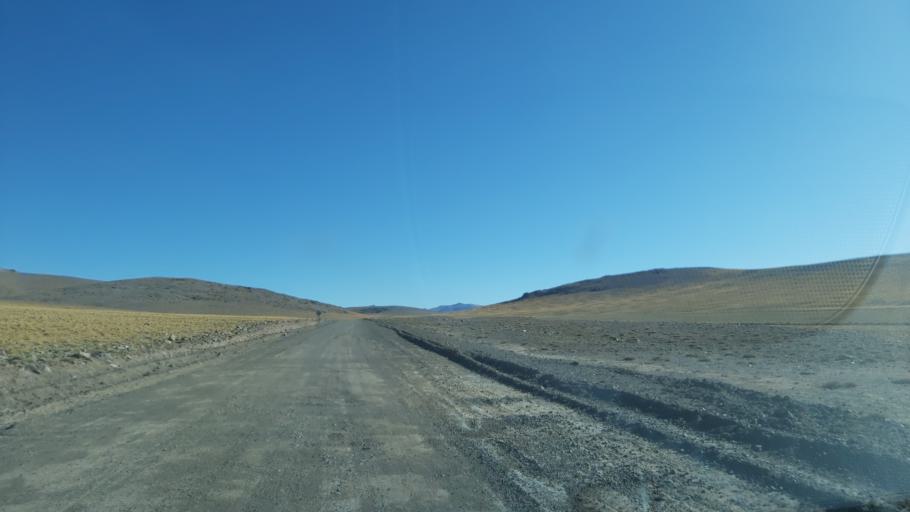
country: CL
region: Atacama
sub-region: Provincia de Chanaral
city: Diego de Almagro
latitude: -26.4567
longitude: -69.2906
